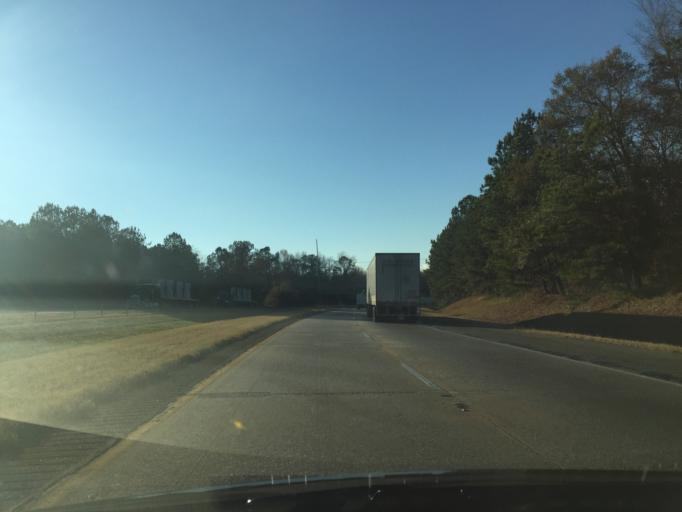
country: US
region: Georgia
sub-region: Bibb County
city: West Point
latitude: 32.9400
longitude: -83.7789
